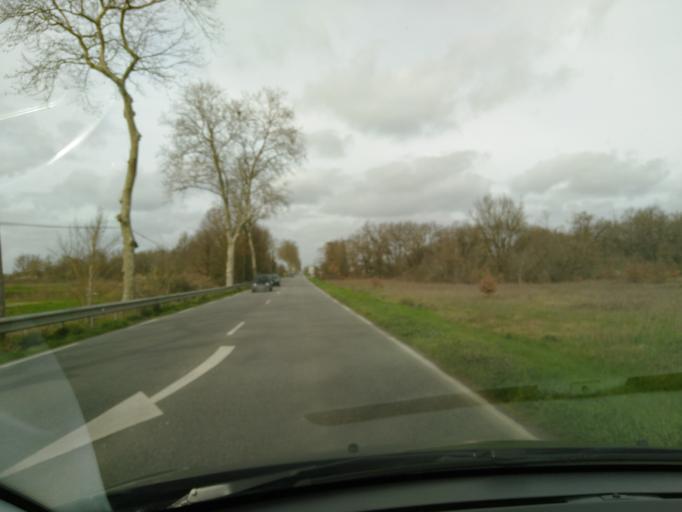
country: FR
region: Midi-Pyrenees
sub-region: Departement de la Haute-Garonne
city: Merville
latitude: 43.7221
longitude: 1.3284
